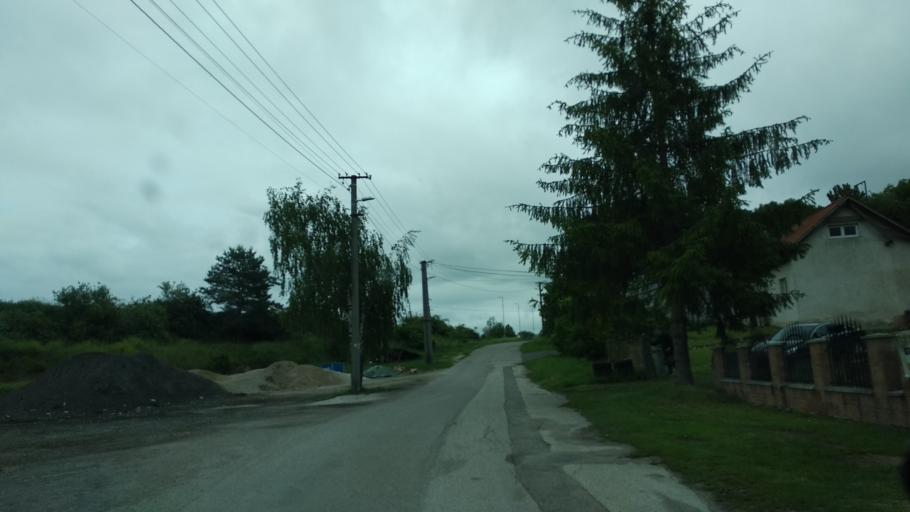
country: SK
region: Trenciansky
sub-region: Okres Trencin
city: Trencin
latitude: 48.8023
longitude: 18.1153
